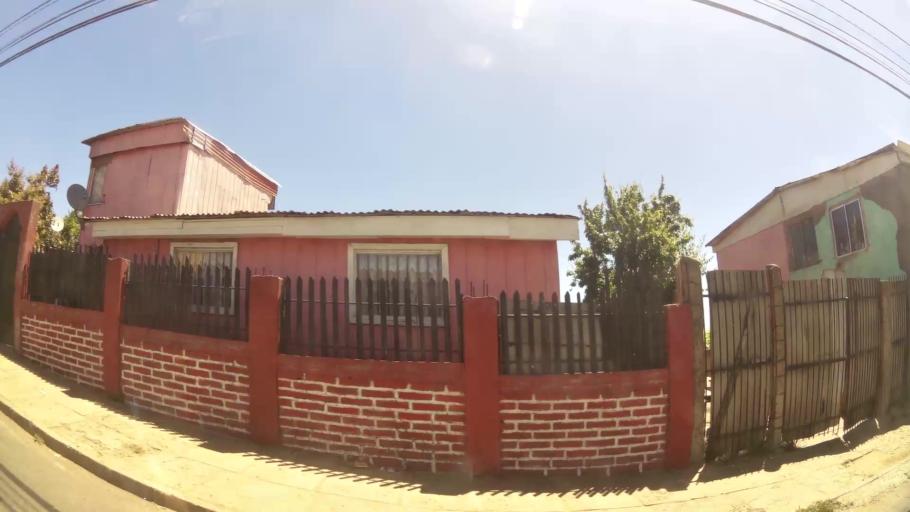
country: CL
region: Valparaiso
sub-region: Provincia de Valparaiso
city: Valparaiso
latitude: -33.0578
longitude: -71.6393
